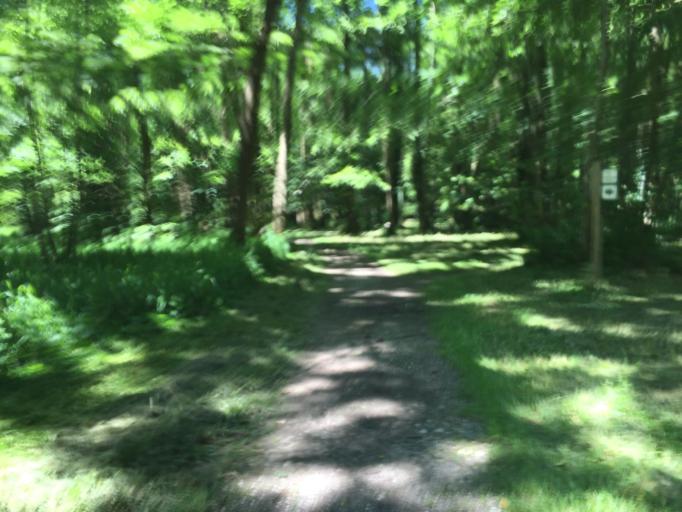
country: FR
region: Rhone-Alpes
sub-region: Departement de la Savoie
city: Le Bourget-du-Lac
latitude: 45.6476
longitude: 5.8697
